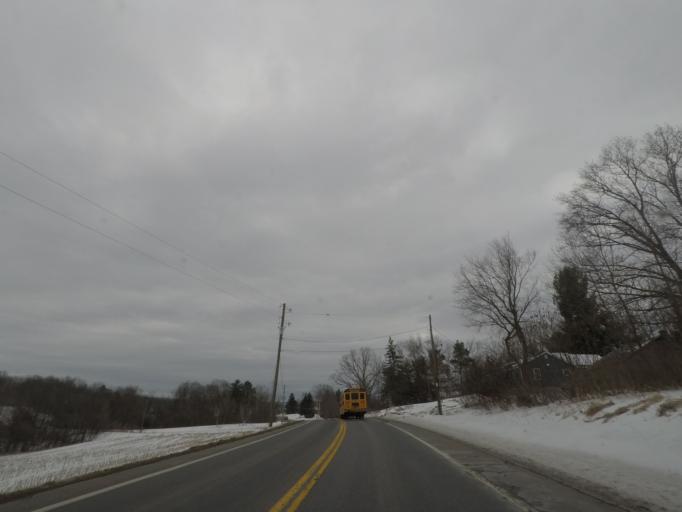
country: US
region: New York
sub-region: Saratoga County
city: Stillwater
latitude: 42.9586
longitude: -73.6744
